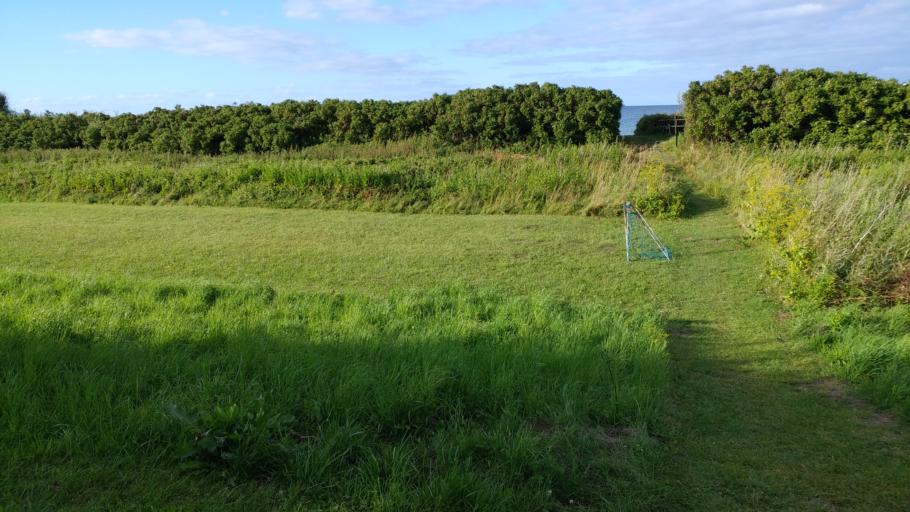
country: DK
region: South Denmark
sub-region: Nordfyns Kommune
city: Otterup
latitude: 55.5790
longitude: 10.4316
